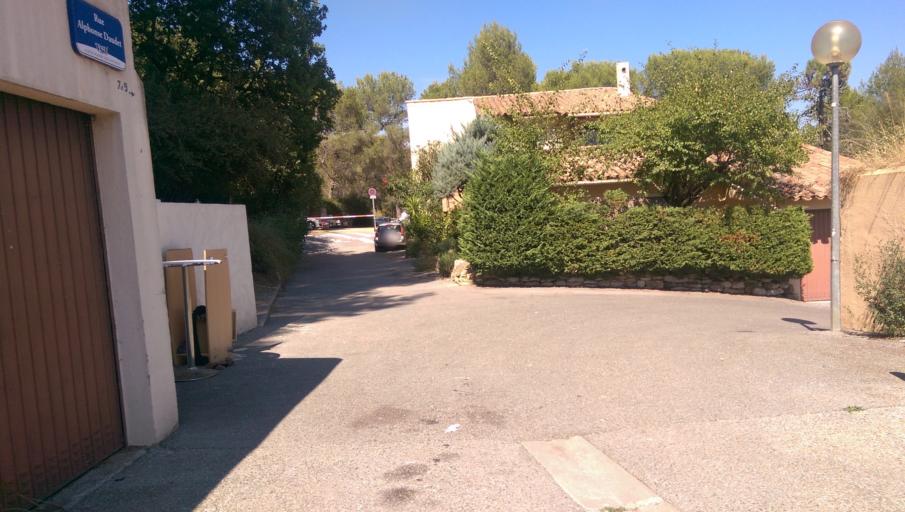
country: FR
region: Provence-Alpes-Cote d'Azur
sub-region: Departement des Alpes-Maritimes
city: Valbonne
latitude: 43.6240
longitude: 7.0418
